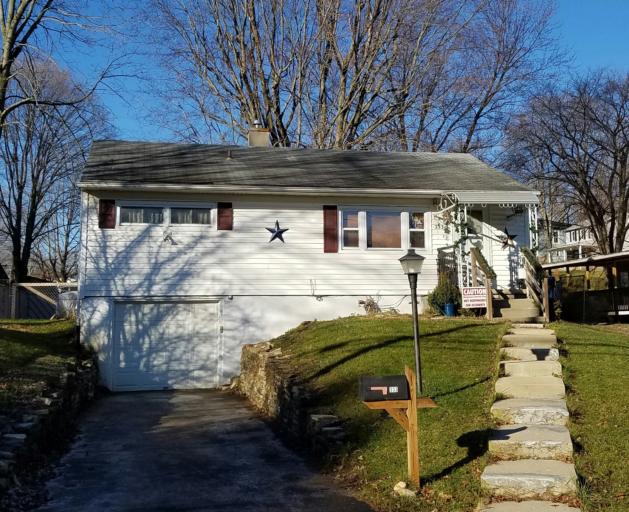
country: US
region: Ohio
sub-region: Morrow County
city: Mount Gilead
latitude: 40.5532
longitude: -82.8221
